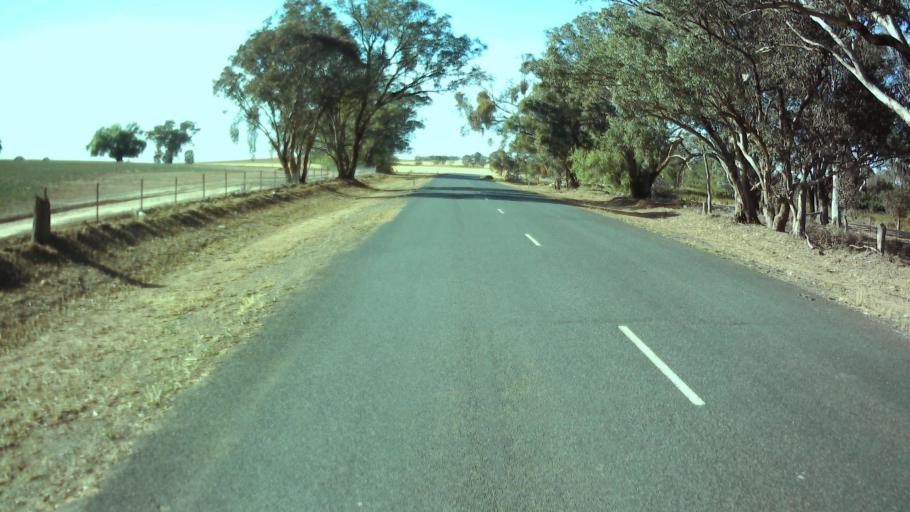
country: AU
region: New South Wales
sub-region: Weddin
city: Grenfell
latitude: -33.9830
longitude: 148.1405
